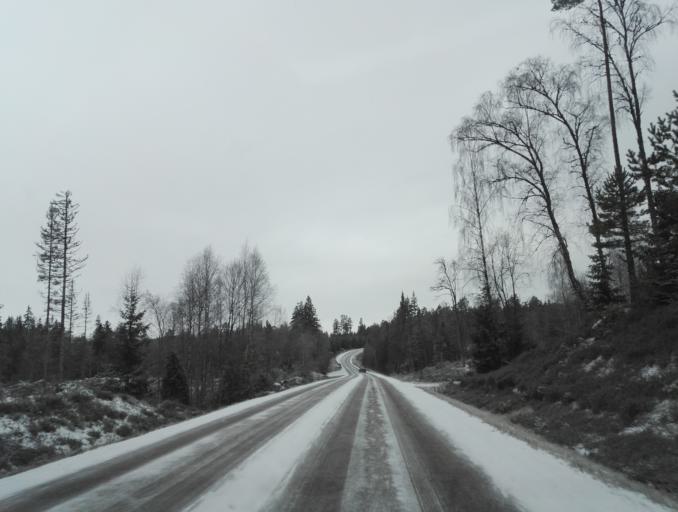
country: SE
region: Kronoberg
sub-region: Lessebo Kommun
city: Lessebo
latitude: 56.8089
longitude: 15.3666
